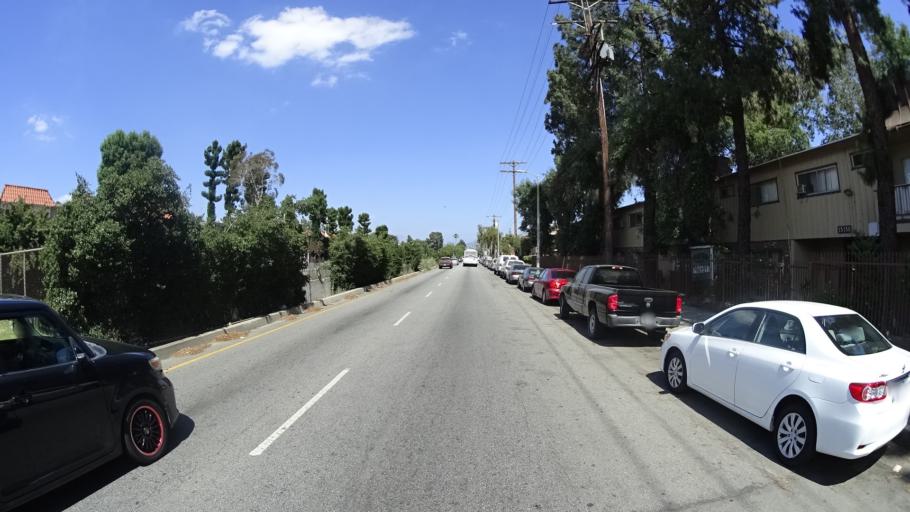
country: US
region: California
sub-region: Los Angeles County
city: Van Nuys
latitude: 34.2282
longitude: -118.4631
